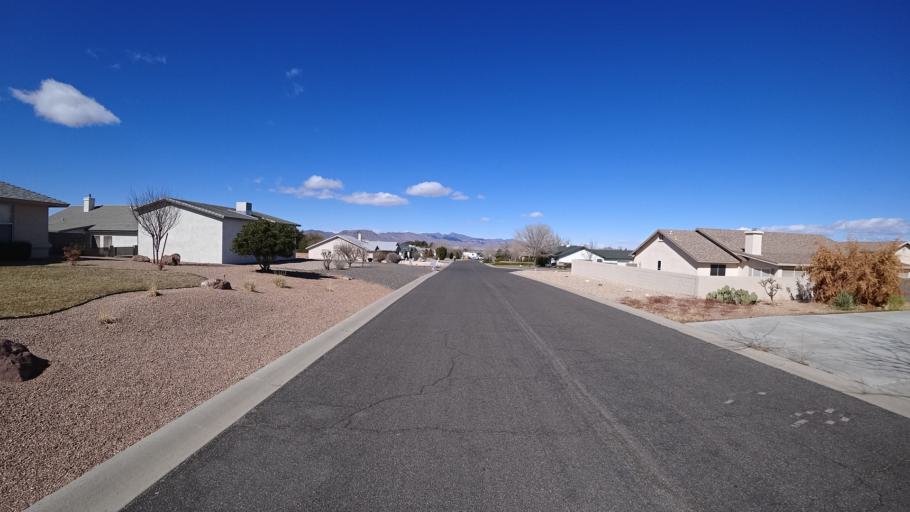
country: US
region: Arizona
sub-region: Mohave County
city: Kingman
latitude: 35.2007
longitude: -113.9654
